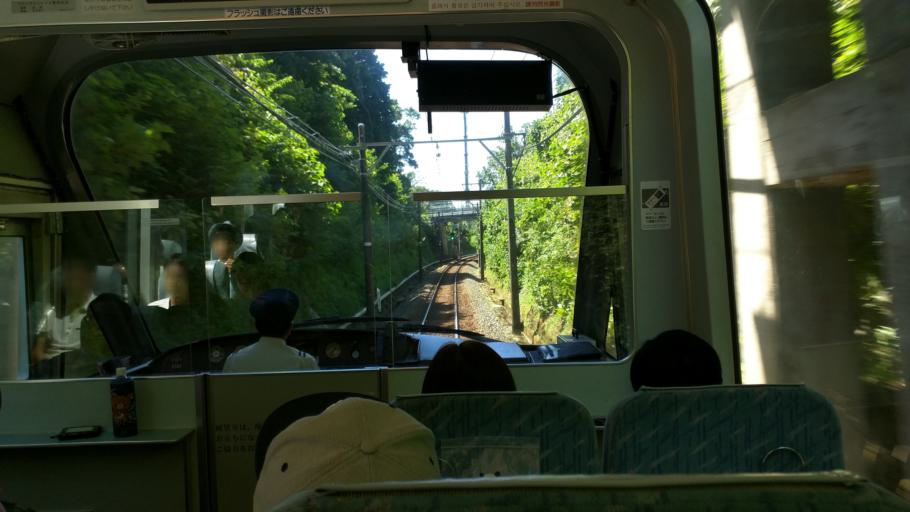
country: JP
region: Shizuoka
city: Ito
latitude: 34.9258
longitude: 139.1359
